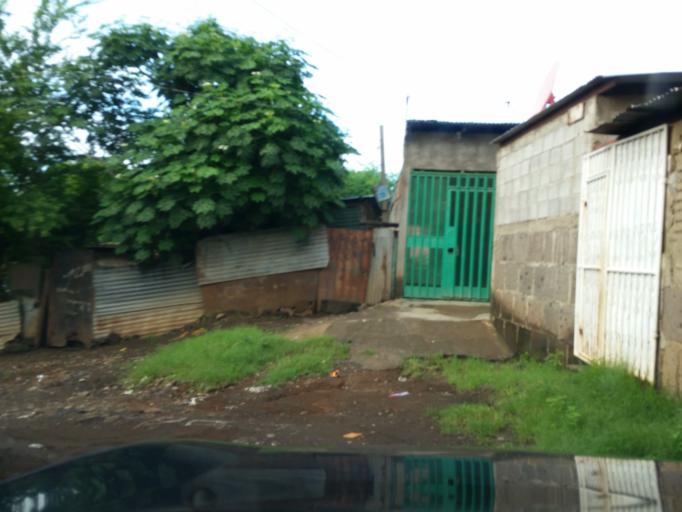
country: NI
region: Managua
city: Managua
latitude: 12.1125
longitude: -86.2047
